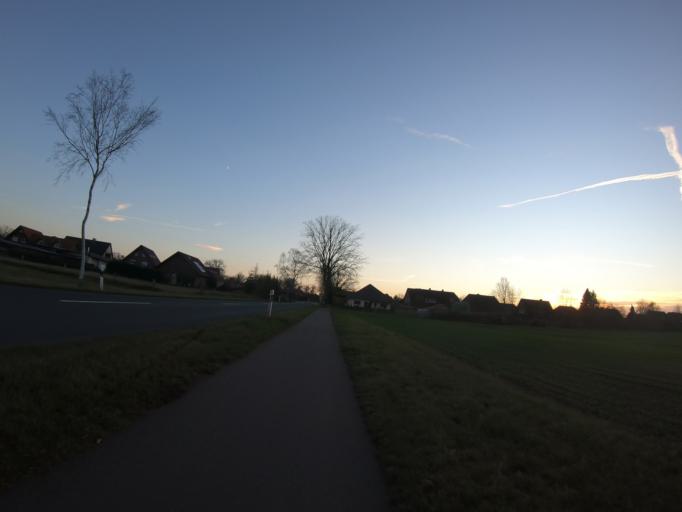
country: DE
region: Lower Saxony
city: Wagenhoff
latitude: 52.4947
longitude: 10.4752
